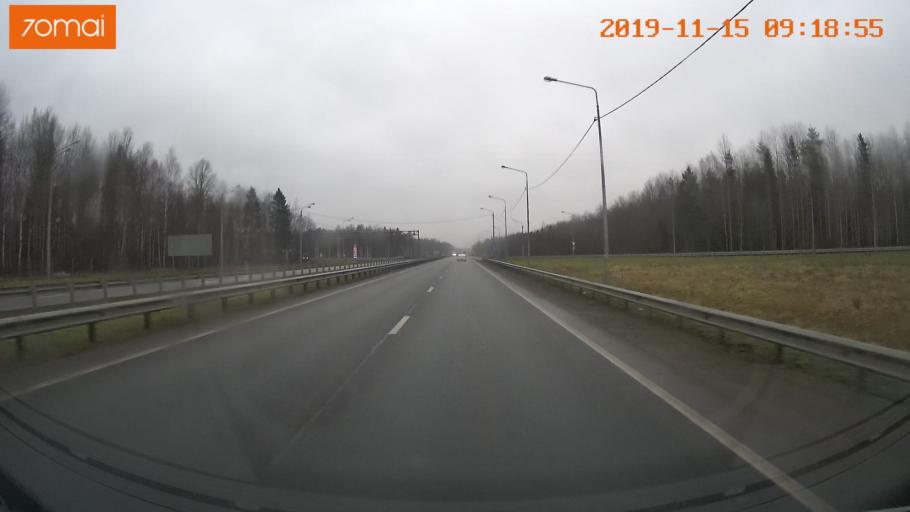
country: RU
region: Vologda
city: Tonshalovo
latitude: 59.2792
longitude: 38.0059
